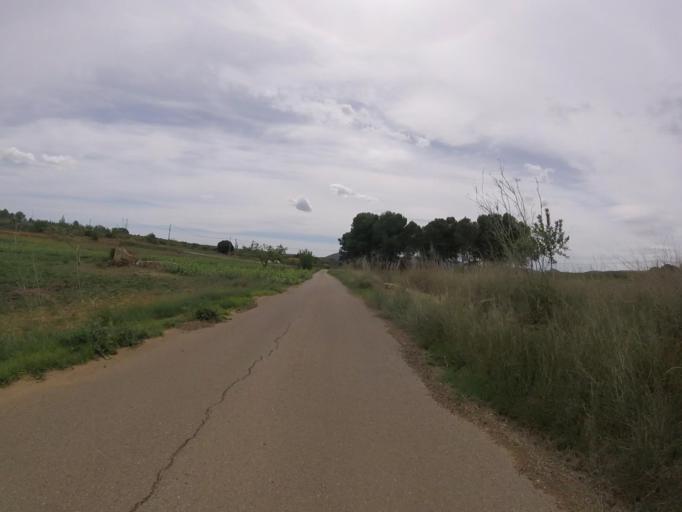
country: ES
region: Valencia
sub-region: Provincia de Castello
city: Benlloch
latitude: 40.1784
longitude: -0.0060
